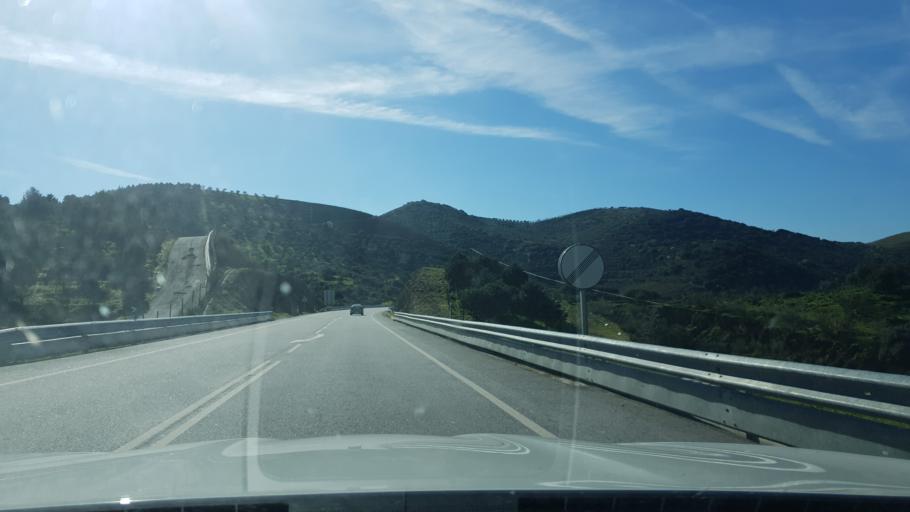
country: PT
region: Braganca
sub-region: Torre de Moncorvo
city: Torre de Moncorvo
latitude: 41.2082
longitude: -7.0815
